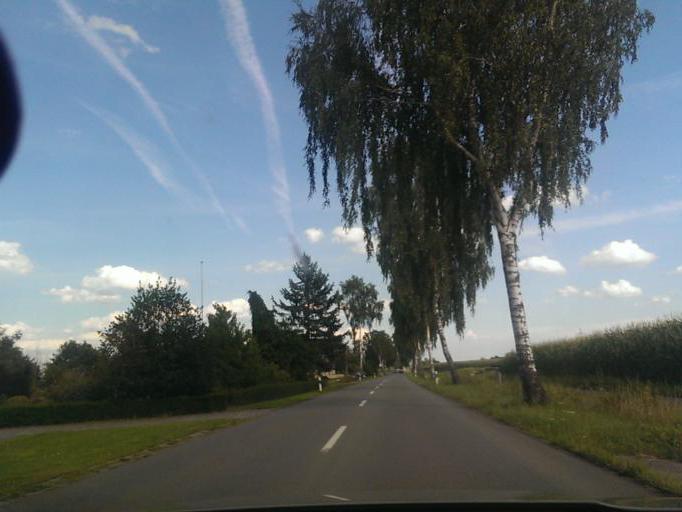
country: DE
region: North Rhine-Westphalia
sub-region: Regierungsbezirk Detmold
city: Delbruck
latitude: 51.7375
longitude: 8.6023
